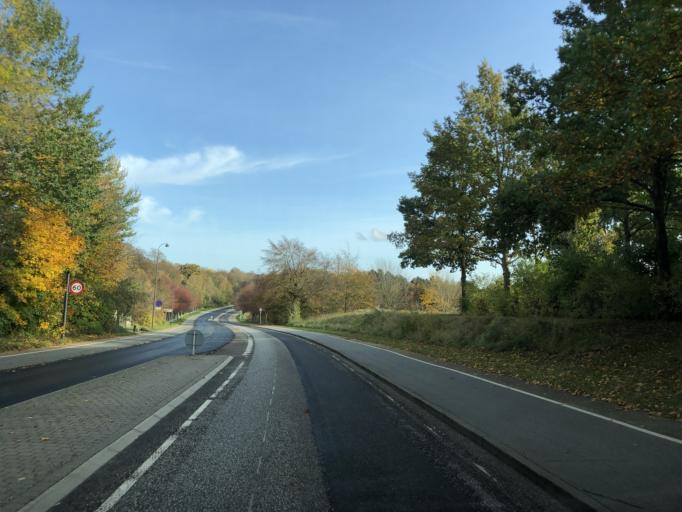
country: DK
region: Capital Region
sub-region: Rudersdal Kommune
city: Birkerod
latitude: 55.8380
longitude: 12.4460
